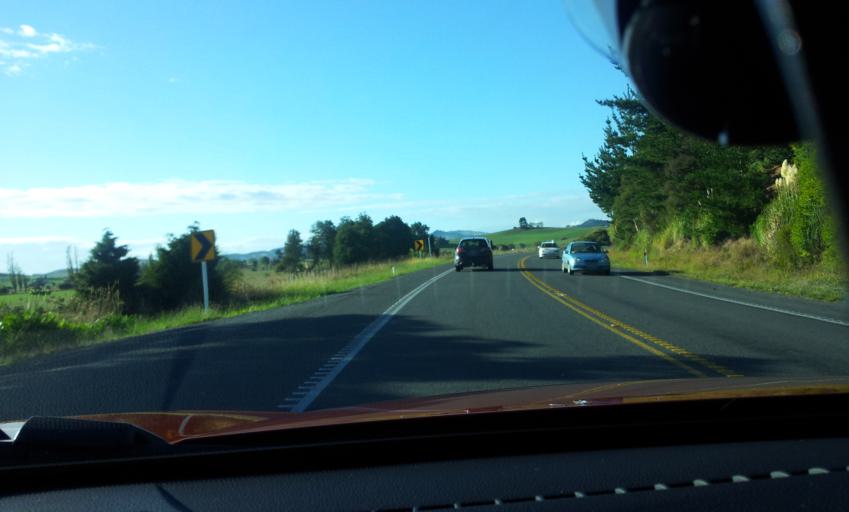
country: NZ
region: Waikato
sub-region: Waikato District
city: Te Kauwhata
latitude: -37.2694
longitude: 175.2803
